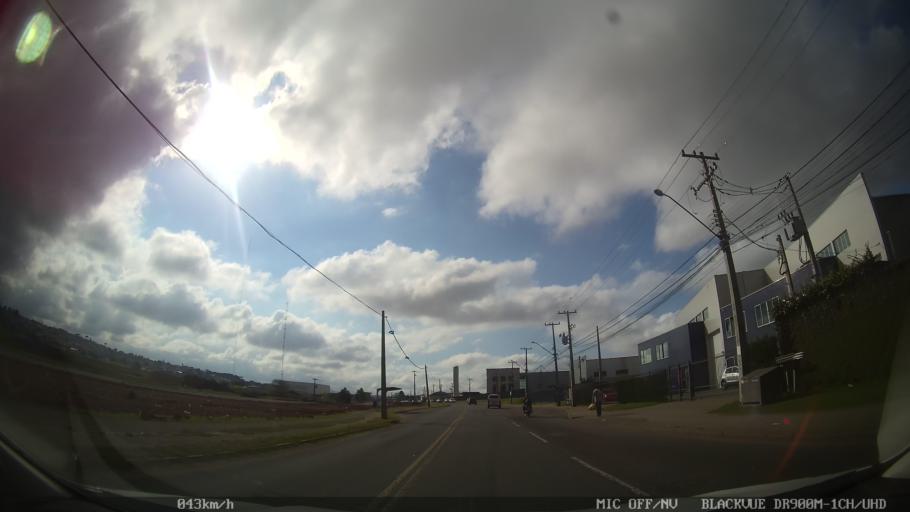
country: BR
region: Parana
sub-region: Pinhais
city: Pinhais
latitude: -25.4092
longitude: -49.1895
